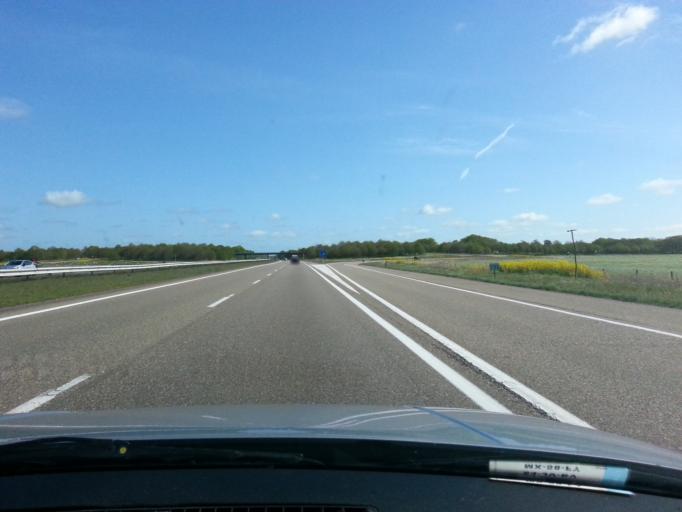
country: NL
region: Friesland
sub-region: Gemeente Smallingerland
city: Boornbergum
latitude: 53.0596
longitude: 6.0502
